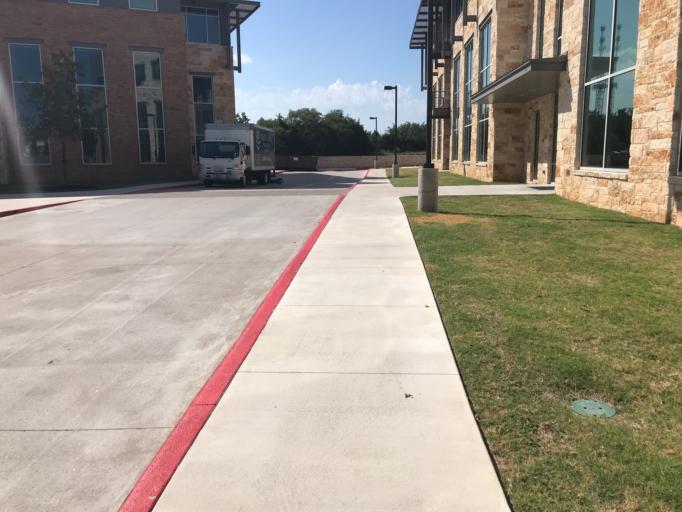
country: US
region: Texas
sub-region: Travis County
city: Bee Cave
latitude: 30.3138
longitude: -97.9457
